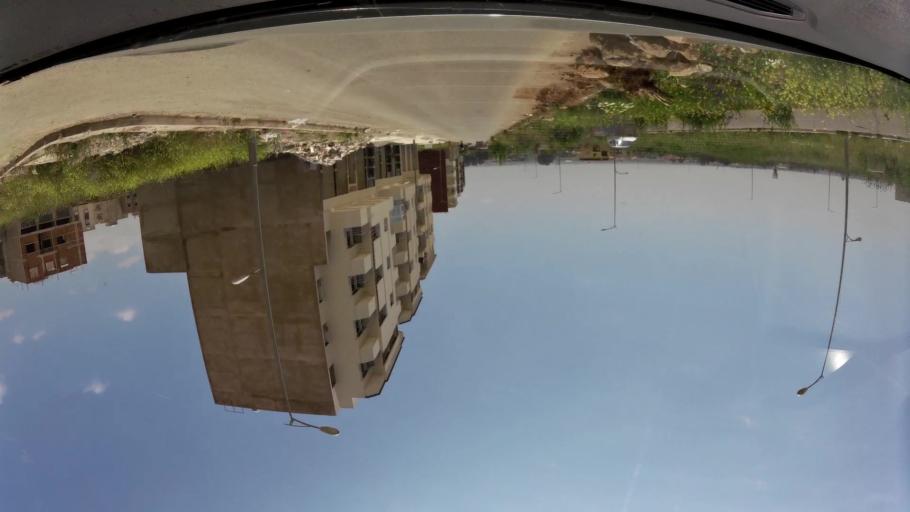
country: MA
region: Fes-Boulemane
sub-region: Fes
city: Fes
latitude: 34.0512
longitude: -5.0410
